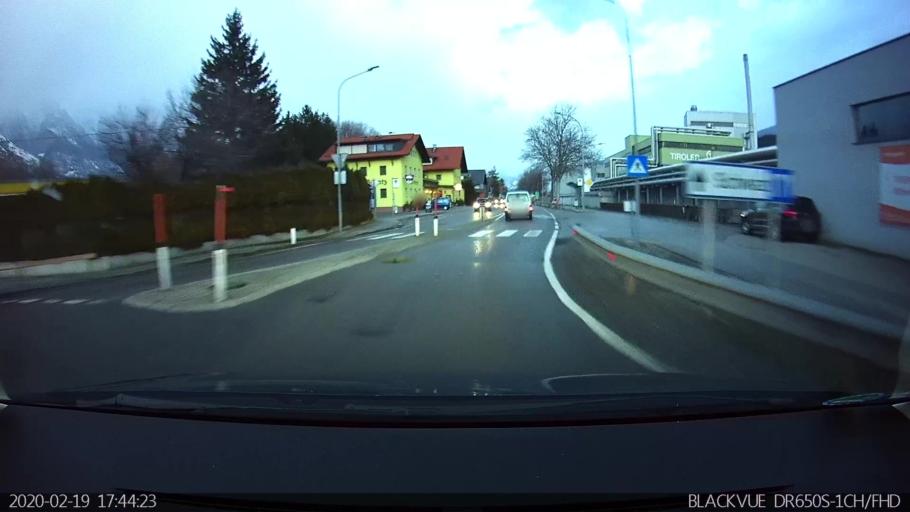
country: AT
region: Tyrol
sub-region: Politischer Bezirk Innsbruck Land
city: Absam
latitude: 47.2770
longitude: 11.4865
